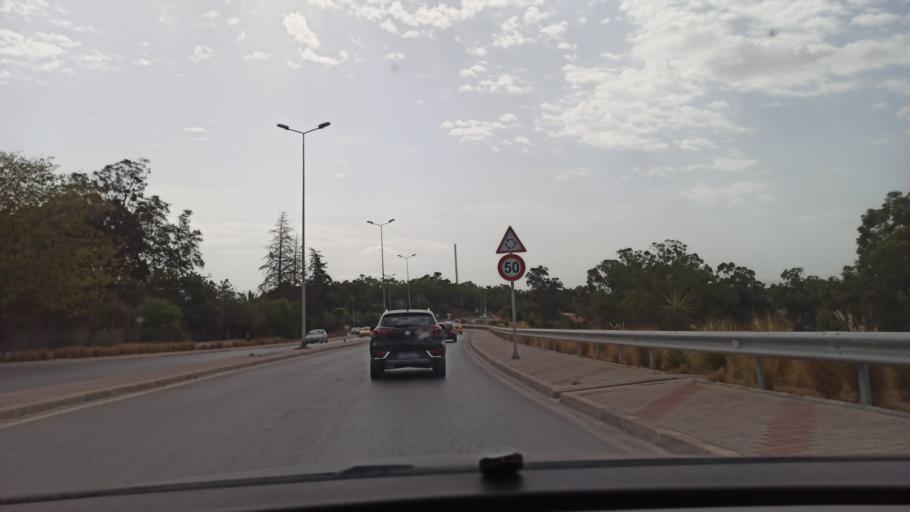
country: TN
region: Tunis
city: Tunis
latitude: 36.8295
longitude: 10.1652
